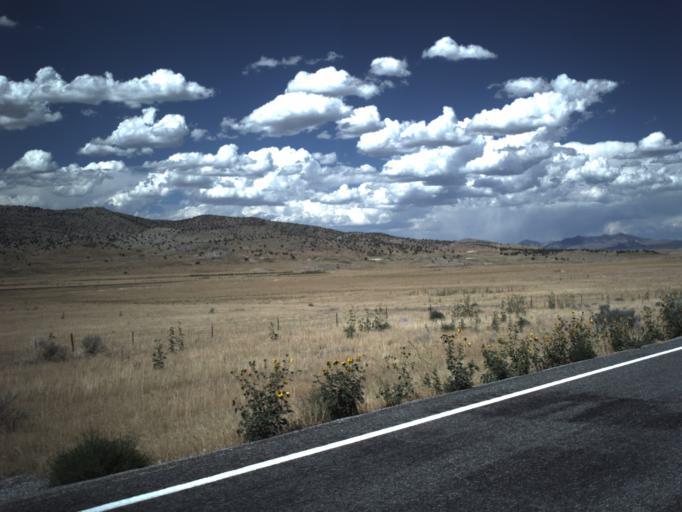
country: US
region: Utah
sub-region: Millard County
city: Delta
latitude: 39.6525
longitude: -112.2921
